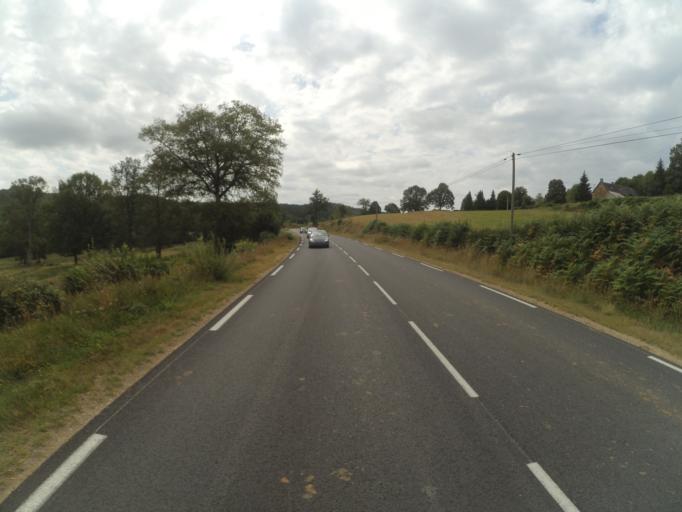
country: FR
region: Limousin
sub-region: Departement de la Creuse
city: La Courtine
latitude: 45.6369
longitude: 2.2761
